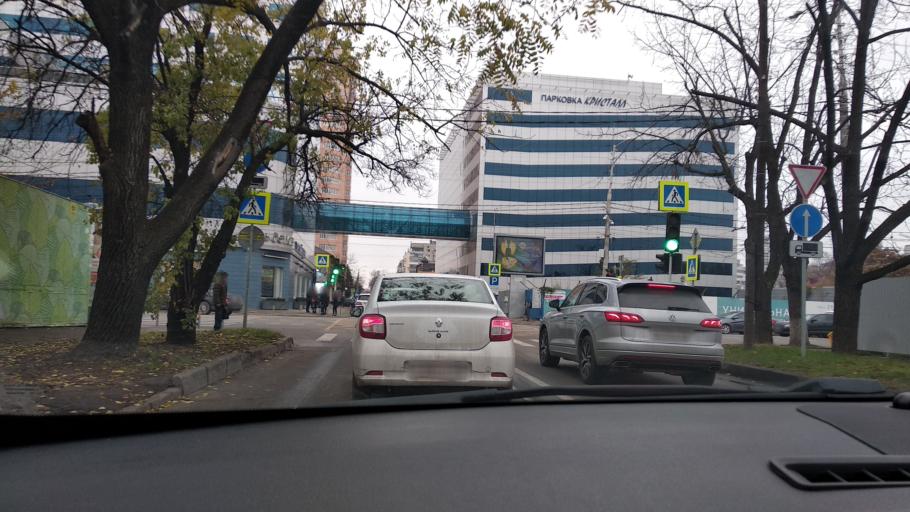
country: RU
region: Krasnodarskiy
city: Krasnodar
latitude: 45.0382
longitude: 38.9865
